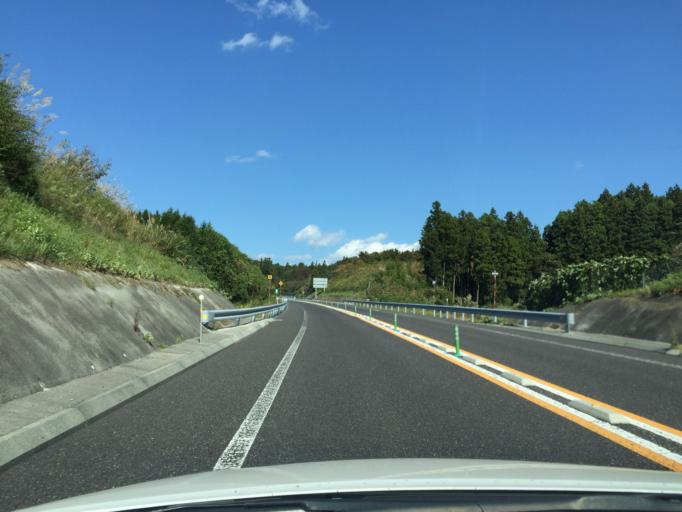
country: JP
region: Fukushima
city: Ishikawa
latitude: 37.2326
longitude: 140.5549
